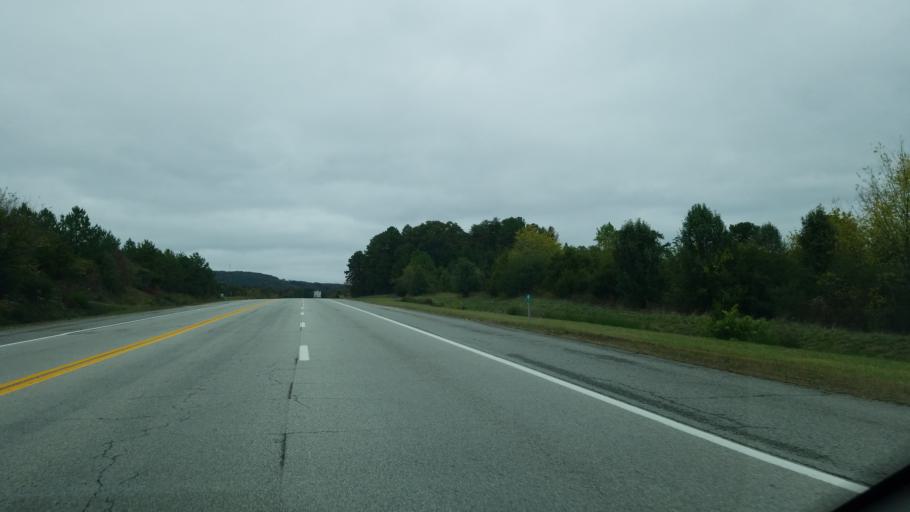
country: US
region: Tennessee
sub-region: Rhea County
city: Dayton
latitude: 35.4631
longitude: -85.0163
